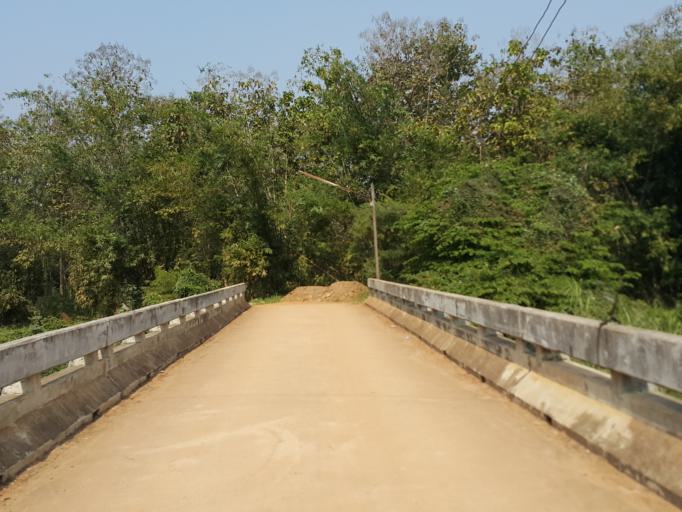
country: TH
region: Sukhothai
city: Thung Saliam
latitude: 17.3219
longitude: 99.5134
